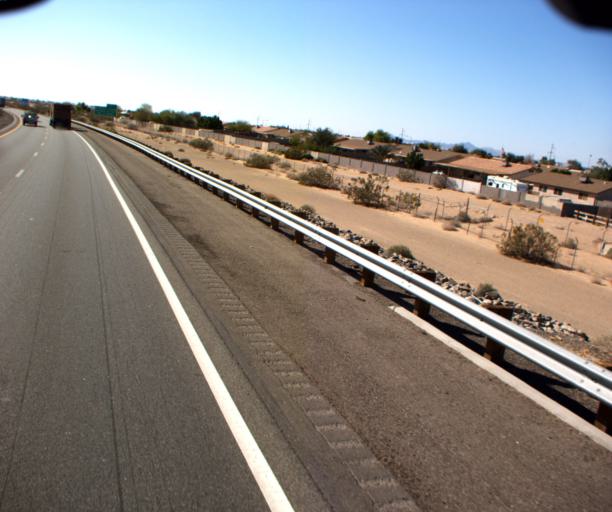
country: US
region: Arizona
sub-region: Yuma County
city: Fortuna Foothills
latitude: 32.6790
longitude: -114.5080
